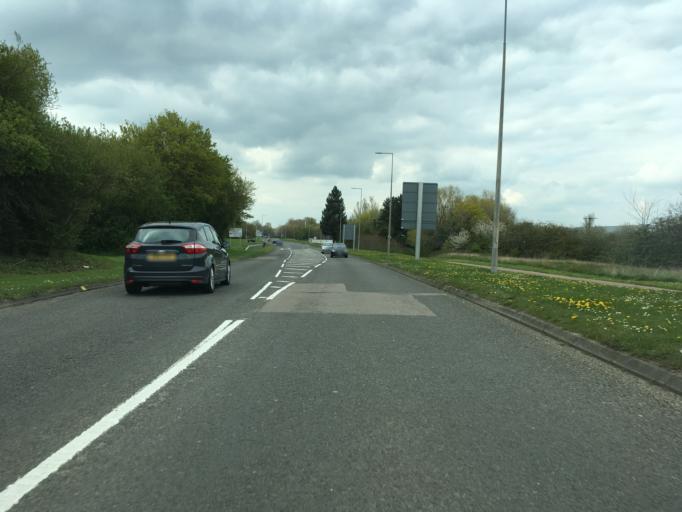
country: GB
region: England
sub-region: Milton Keynes
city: Newport Pagnell
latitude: 52.0636
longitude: -0.7341
